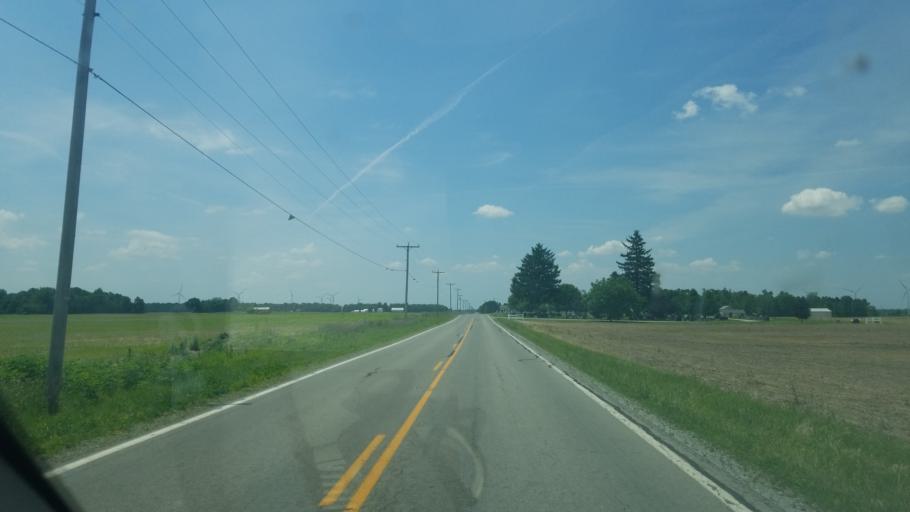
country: US
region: Ohio
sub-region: Hancock County
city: Arlington
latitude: 40.7797
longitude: -83.6720
